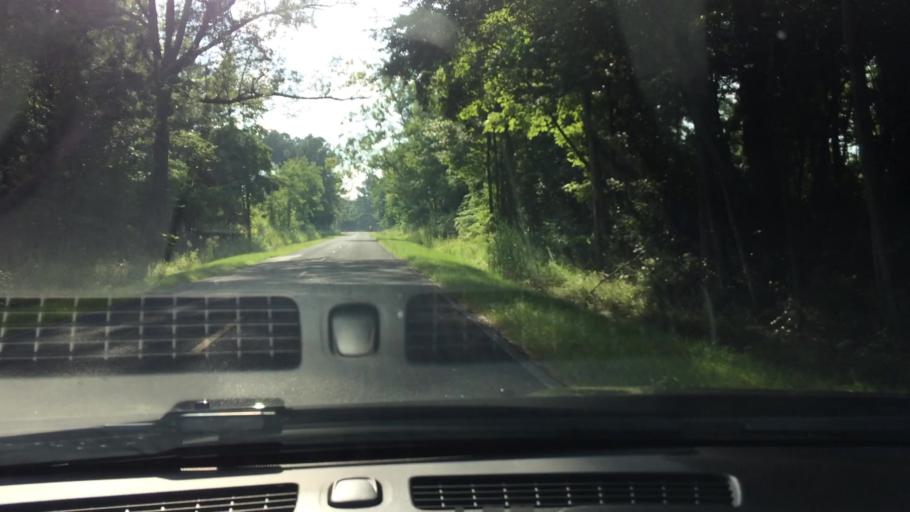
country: US
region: North Carolina
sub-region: Beaufort County
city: River Road
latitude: 35.4580
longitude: -77.0231
